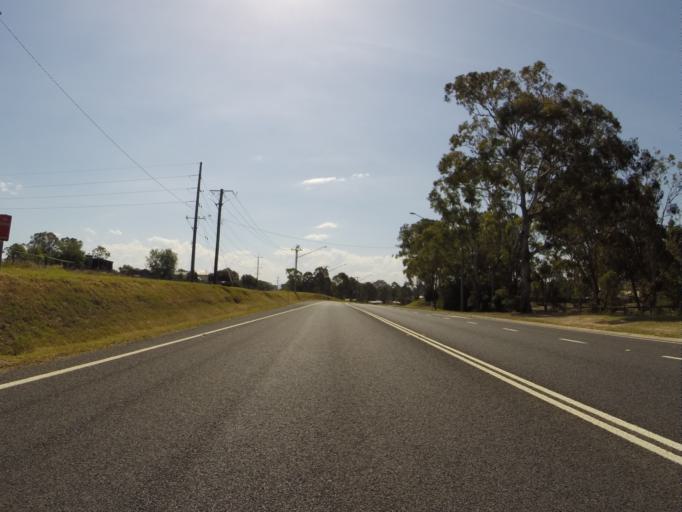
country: AU
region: New South Wales
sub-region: Eurobodalla
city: Moruya
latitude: -35.9228
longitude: 150.0863
